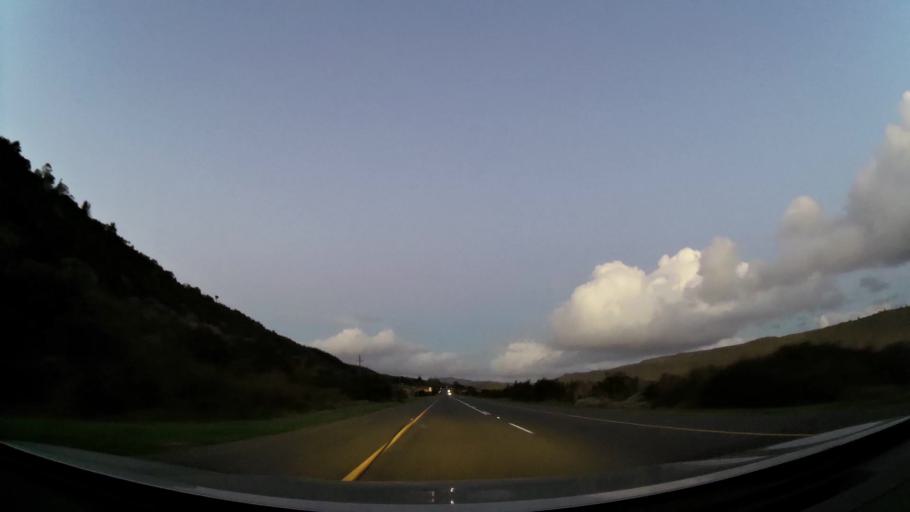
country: ZA
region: Western Cape
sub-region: Eden District Municipality
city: Knysna
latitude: -34.0224
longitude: 22.8410
